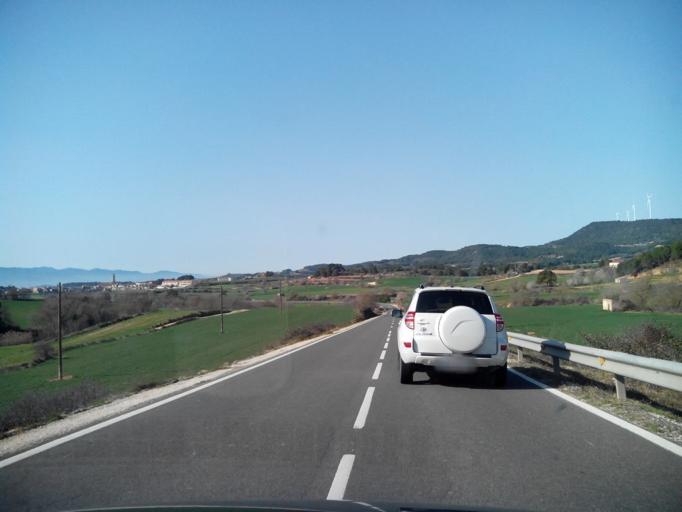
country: ES
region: Catalonia
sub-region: Provincia de Tarragona
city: Conesa
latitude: 41.4844
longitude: 1.2963
